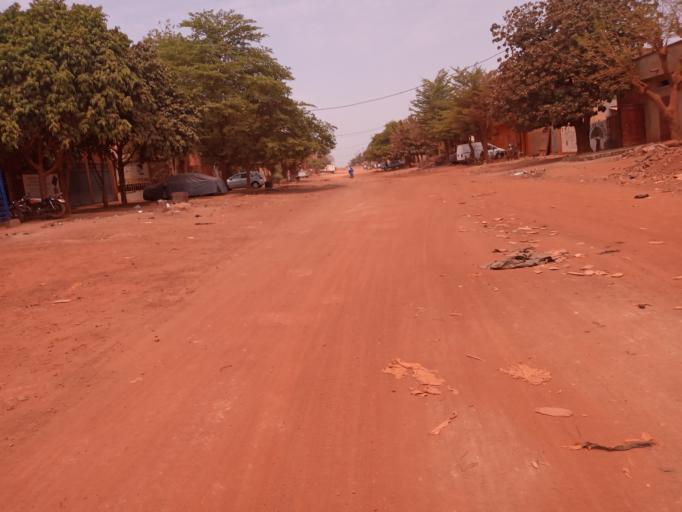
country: ML
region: Bamako
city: Bamako
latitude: 12.5576
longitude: -7.9813
